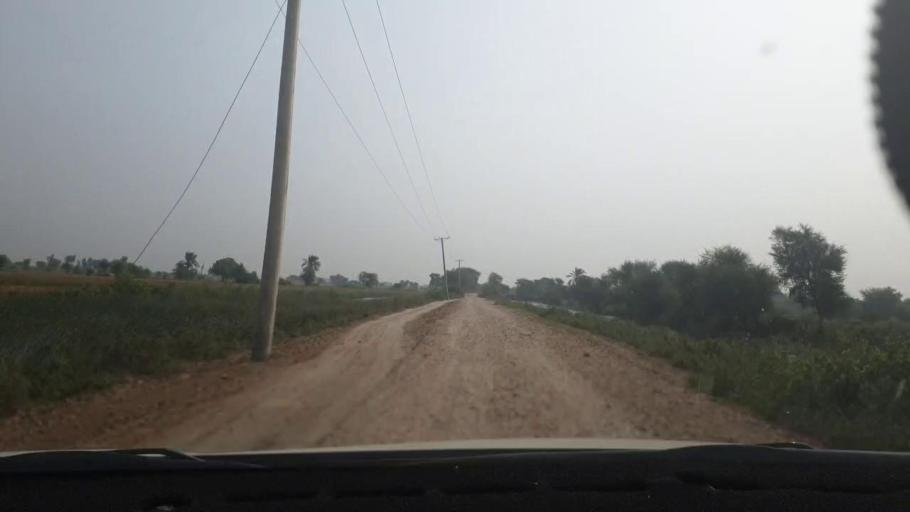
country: PK
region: Sindh
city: Tando Muhammad Khan
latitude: 25.0750
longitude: 68.4982
